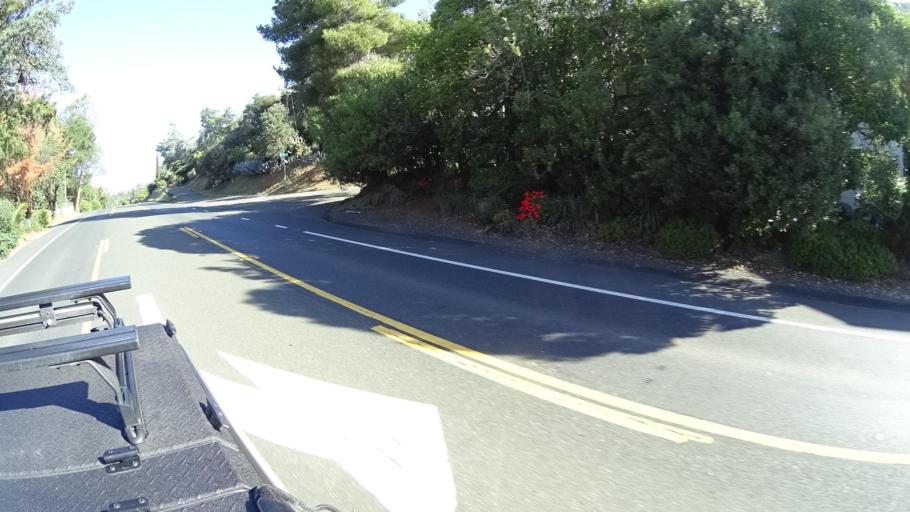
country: US
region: California
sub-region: Lake County
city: Nice
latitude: 39.1189
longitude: -122.8341
